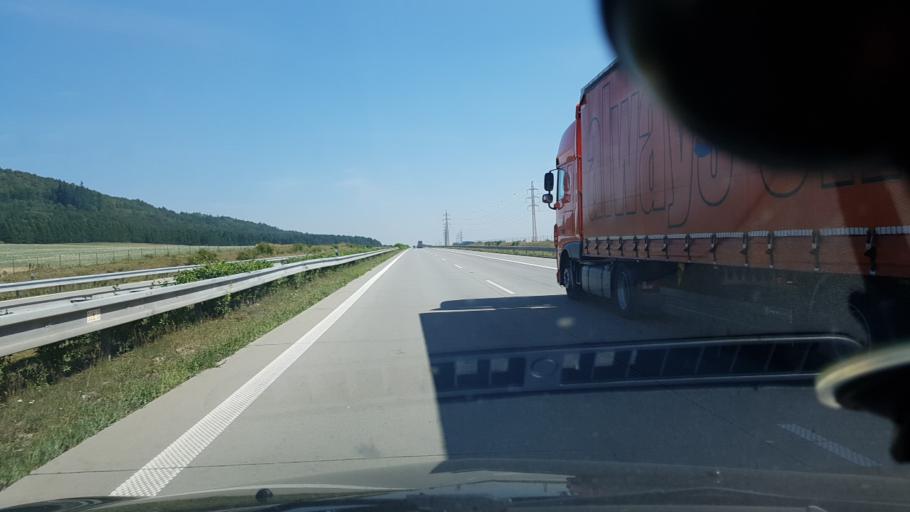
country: CZ
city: Jesenik nad Odrou
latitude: 49.6512
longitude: 17.8876
